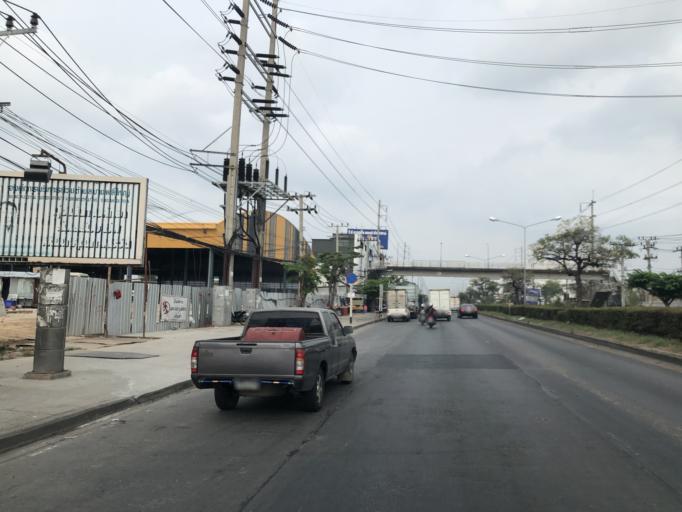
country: TH
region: Bangkok
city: Bang Na
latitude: 13.6079
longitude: 100.6840
